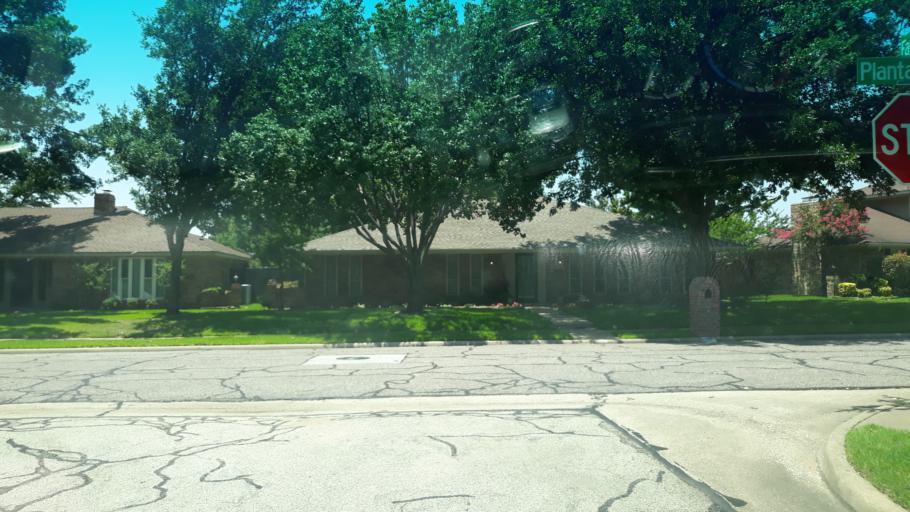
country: US
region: Texas
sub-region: Dallas County
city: Irving
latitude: 32.8522
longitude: -96.9541
